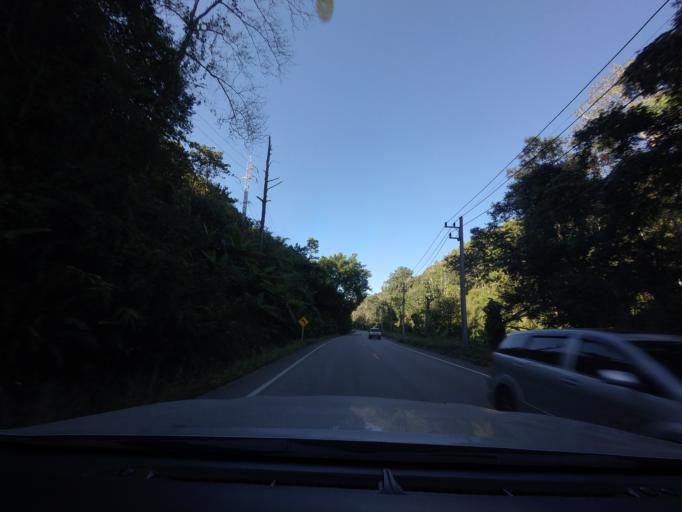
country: TH
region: Chiang Mai
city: Mae Taeng
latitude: 19.1878
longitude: 98.6915
